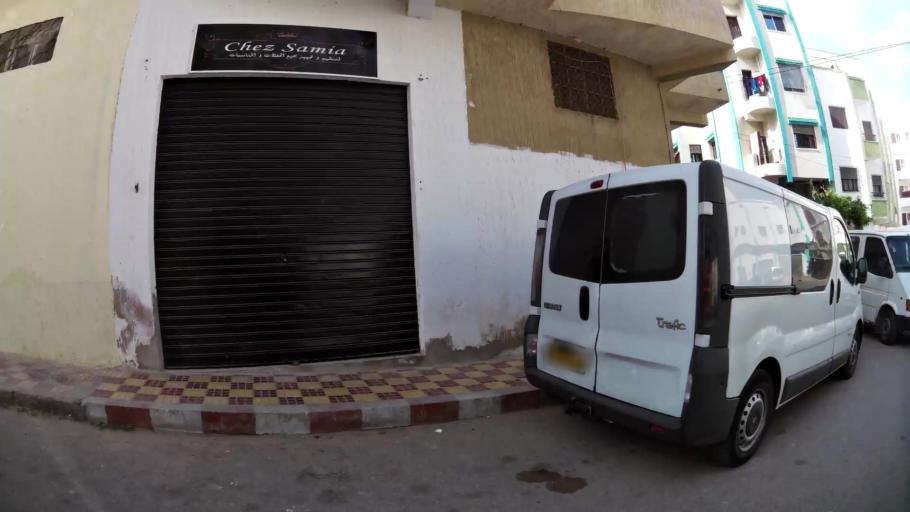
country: MA
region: Tanger-Tetouan
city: Tetouan
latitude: 35.5896
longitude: -5.3492
